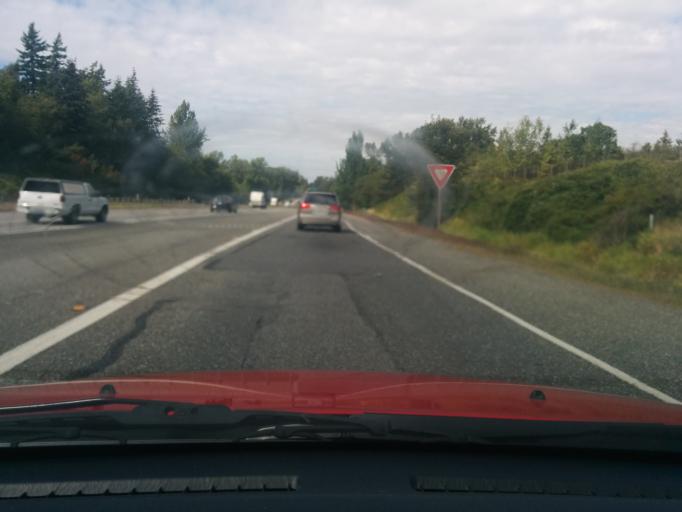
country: US
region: Washington
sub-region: Whatcom County
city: Bellingham
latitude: 48.7737
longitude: -122.4654
